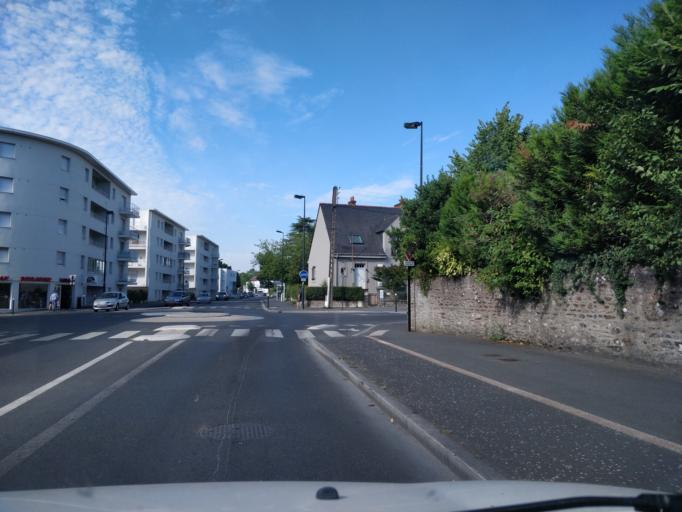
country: FR
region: Pays de la Loire
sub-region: Departement de la Loire-Atlantique
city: Nantes
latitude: 47.2462
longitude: -1.5325
